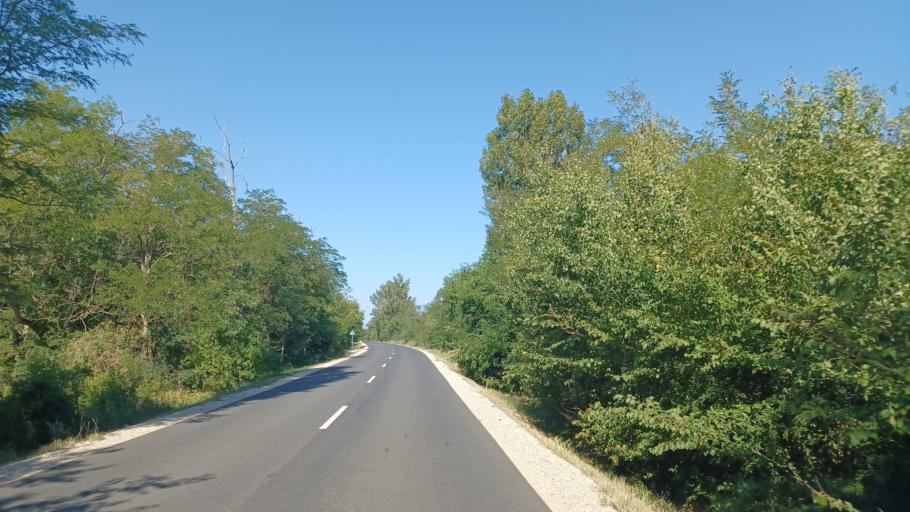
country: HU
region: Fejer
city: Alap
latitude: 46.7443
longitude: 18.6946
